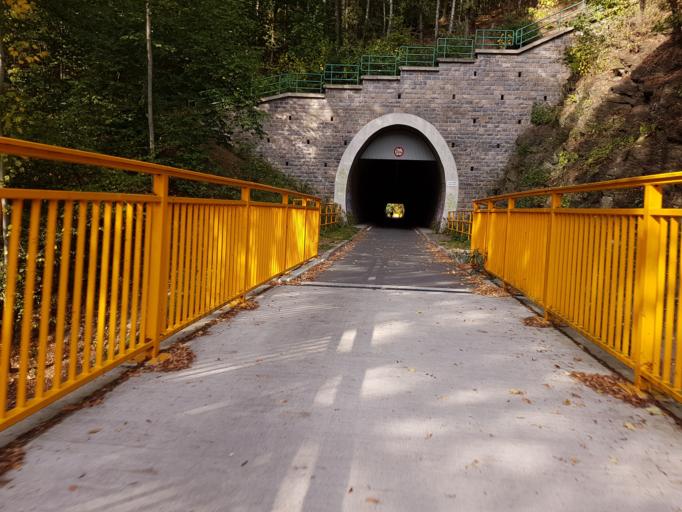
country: DE
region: Saxony
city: Wittgensdorf
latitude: 50.9029
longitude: 12.8953
